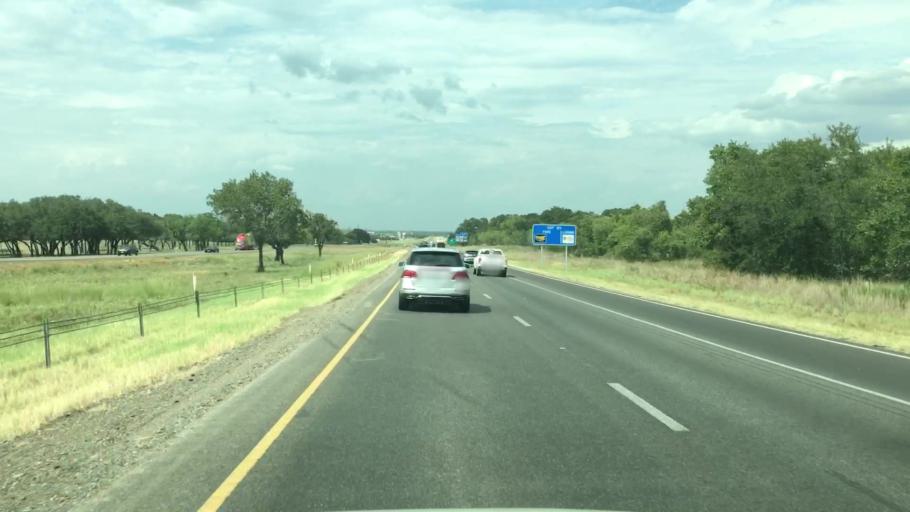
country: US
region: Texas
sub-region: Bexar County
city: Elmendorf
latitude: 29.2004
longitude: -98.4192
